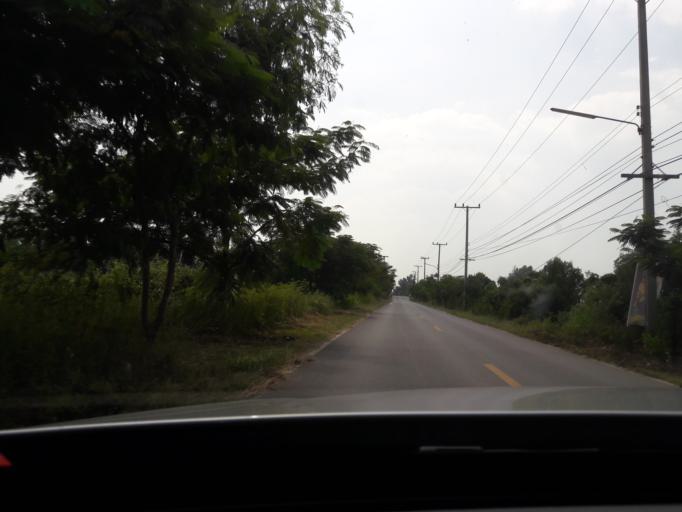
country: TH
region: Samut Songkhram
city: Amphawa
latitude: 13.3334
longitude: 99.9599
